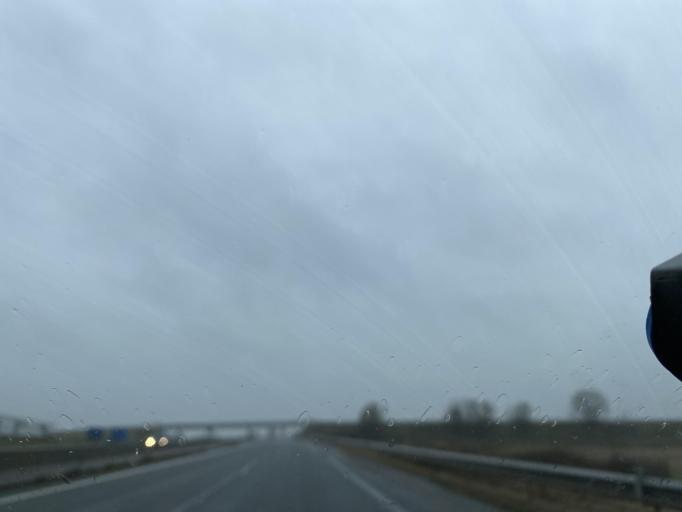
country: FR
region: Centre
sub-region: Departement d'Eure-et-Loir
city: Villemeux-sur-Eure
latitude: 48.5984
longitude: 1.4229
